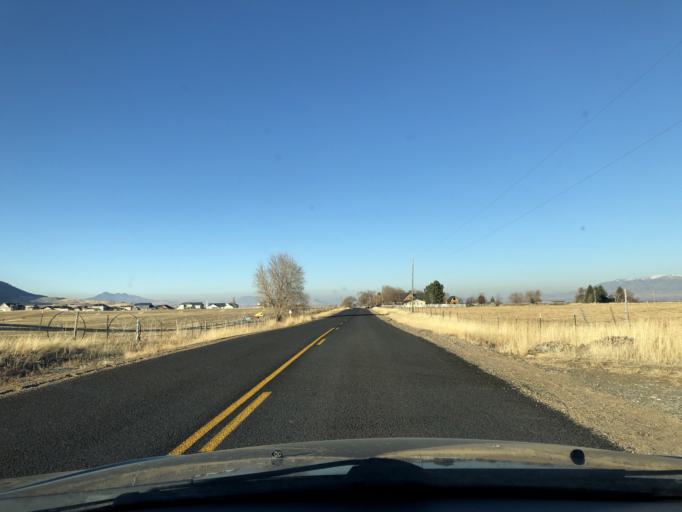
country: US
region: Utah
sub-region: Cache County
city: Wellsville
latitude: 41.6028
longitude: -111.9298
